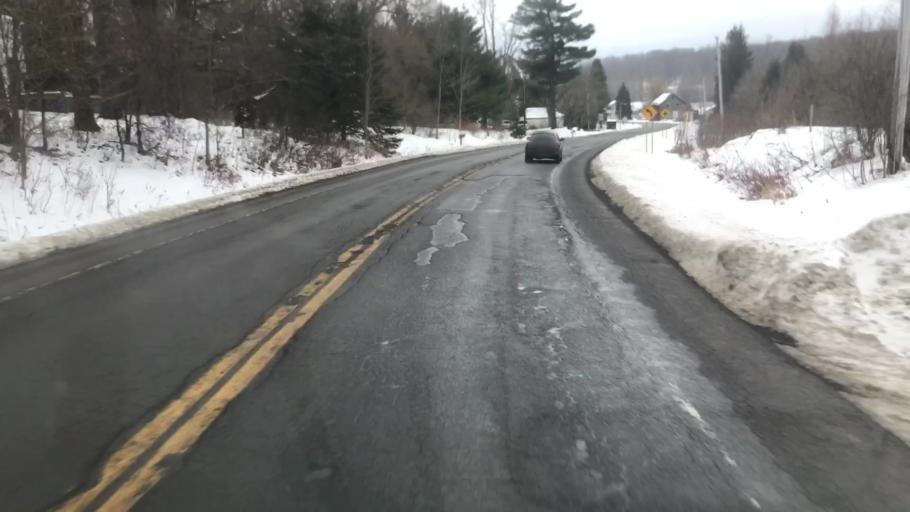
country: US
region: New York
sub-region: Cayuga County
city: Moravia
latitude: 42.7320
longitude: -76.3139
